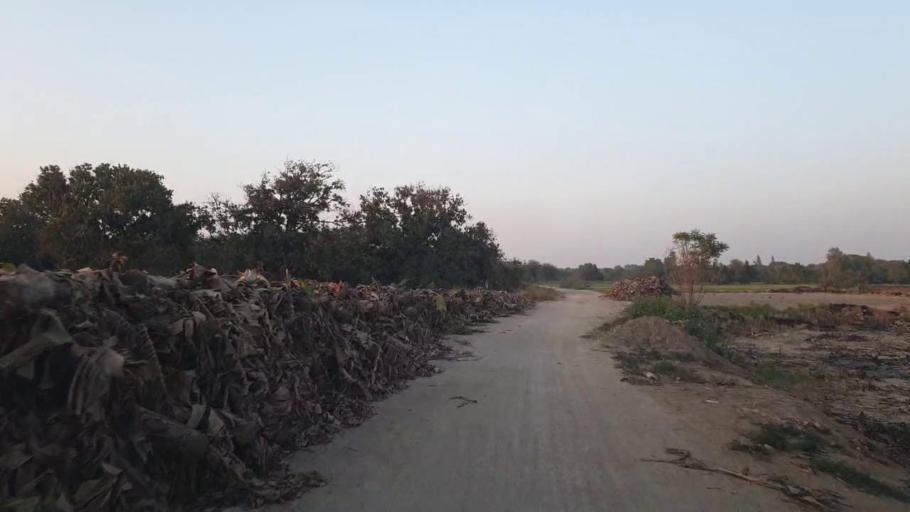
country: PK
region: Sindh
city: Chambar
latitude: 25.4142
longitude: 68.8659
